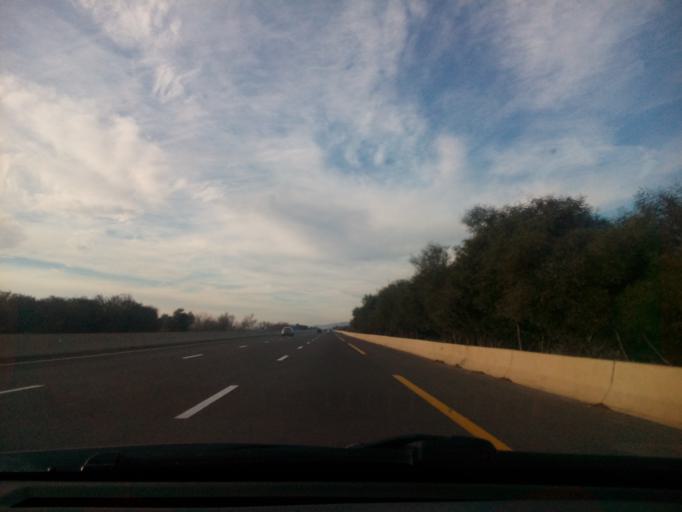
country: DZ
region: Mostaganem
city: Mostaganem
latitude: 35.6804
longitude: 0.1536
